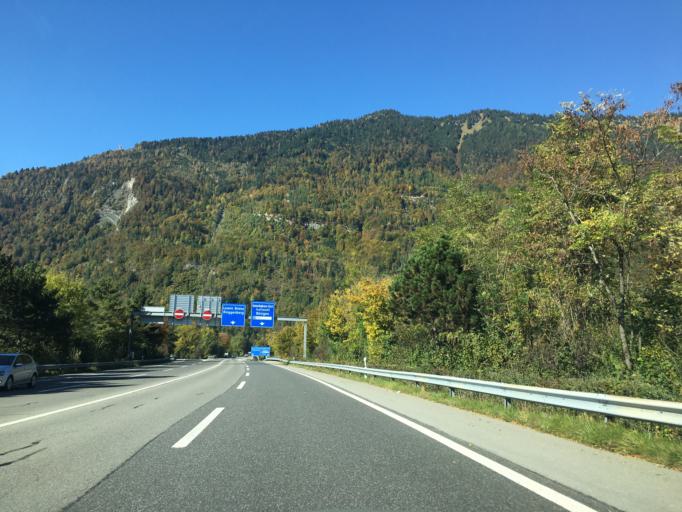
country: CH
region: Bern
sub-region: Interlaken-Oberhasli District
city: Interlaken
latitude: 46.6875
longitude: 7.8774
